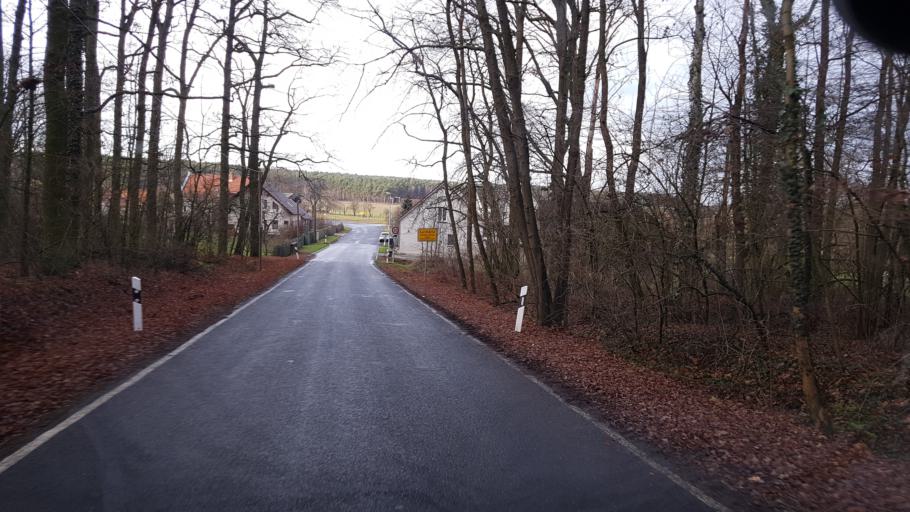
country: DE
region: Brandenburg
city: Altdobern
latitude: 51.6700
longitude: 13.9849
